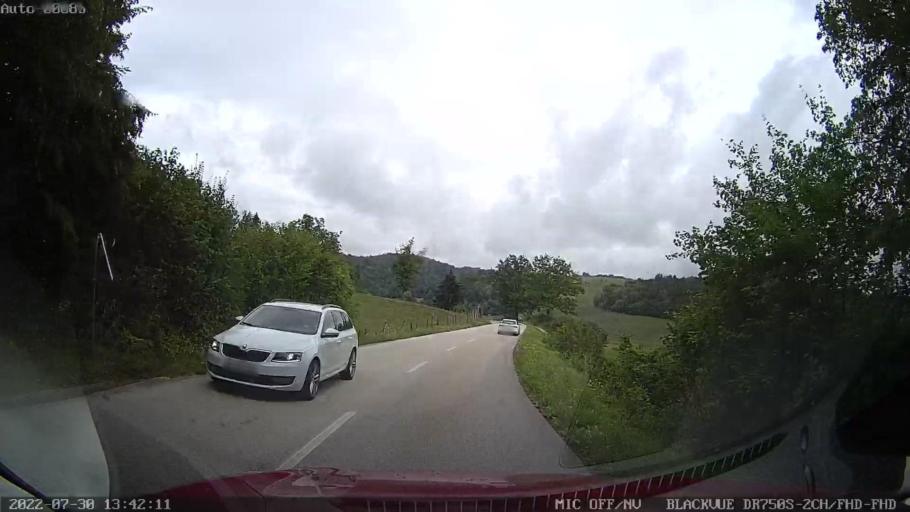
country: SI
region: Ivancna Gorica
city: Sentvid pri Sticni
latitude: 45.9050
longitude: 14.8945
